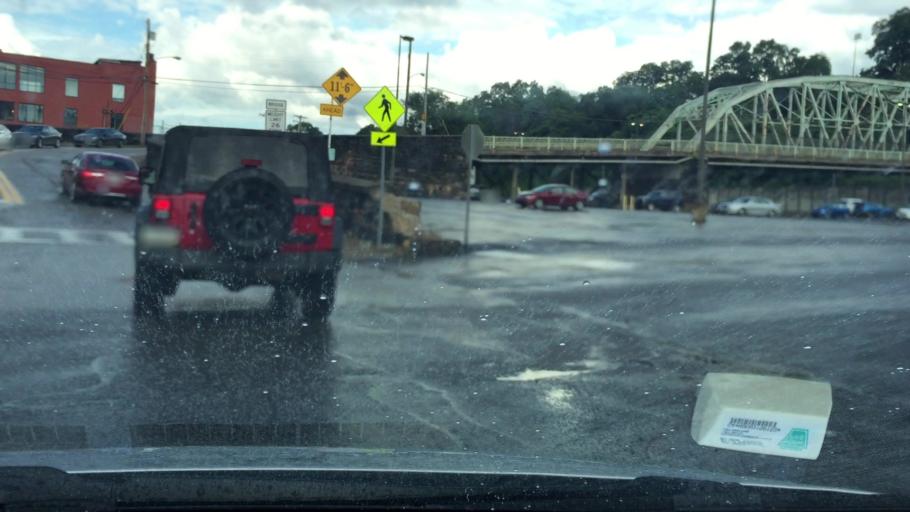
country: US
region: Pennsylvania
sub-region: Allegheny County
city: Millvale
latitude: 40.4561
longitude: -79.9748
